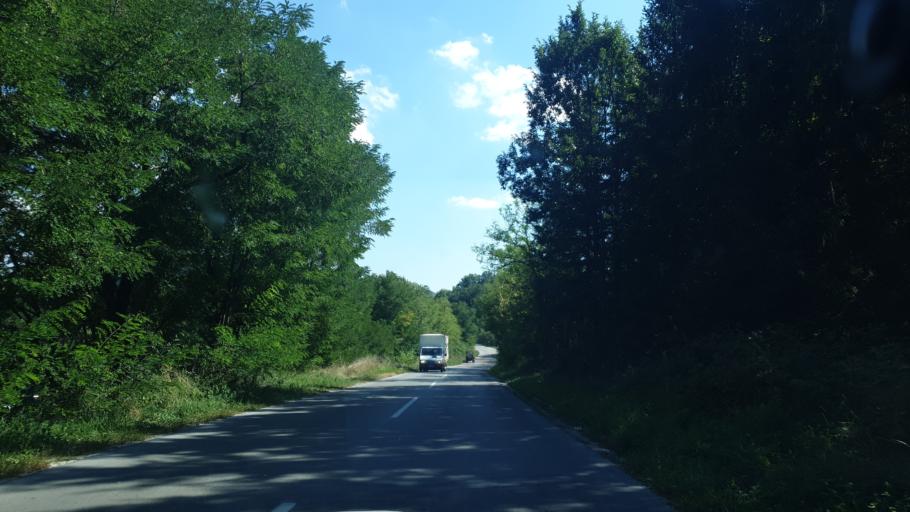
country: RS
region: Central Serbia
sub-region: Zlatiborski Okrug
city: Kosjeric
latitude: 44.0266
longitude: 20.0179
